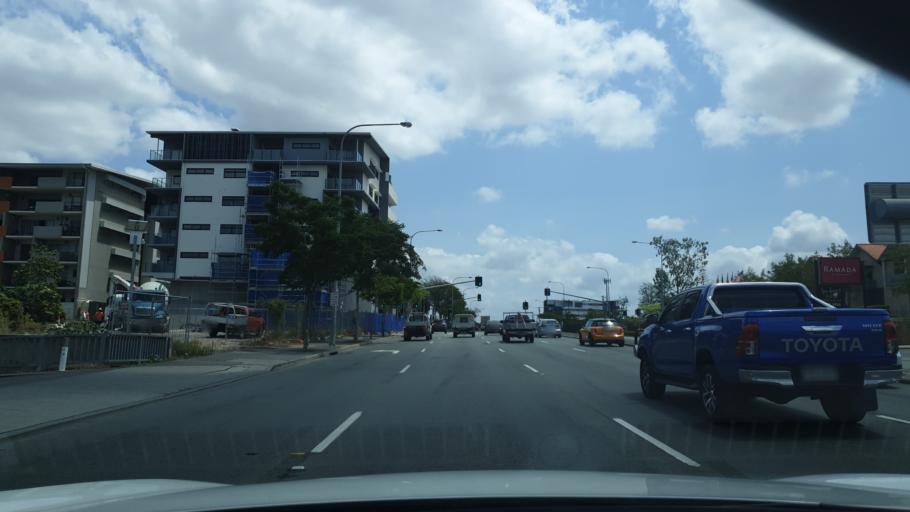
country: AU
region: Queensland
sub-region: Brisbane
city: Windsor
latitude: -27.4391
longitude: 153.0308
